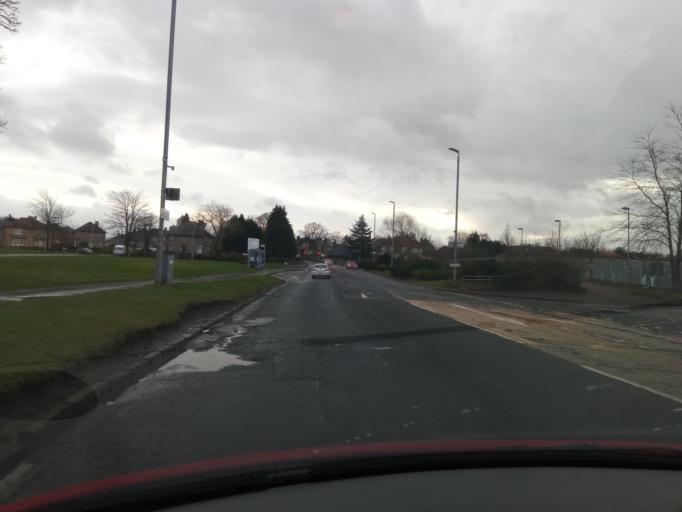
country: GB
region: Scotland
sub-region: East Dunbartonshire
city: Kirkintilloch
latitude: 55.9329
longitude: -4.1536
